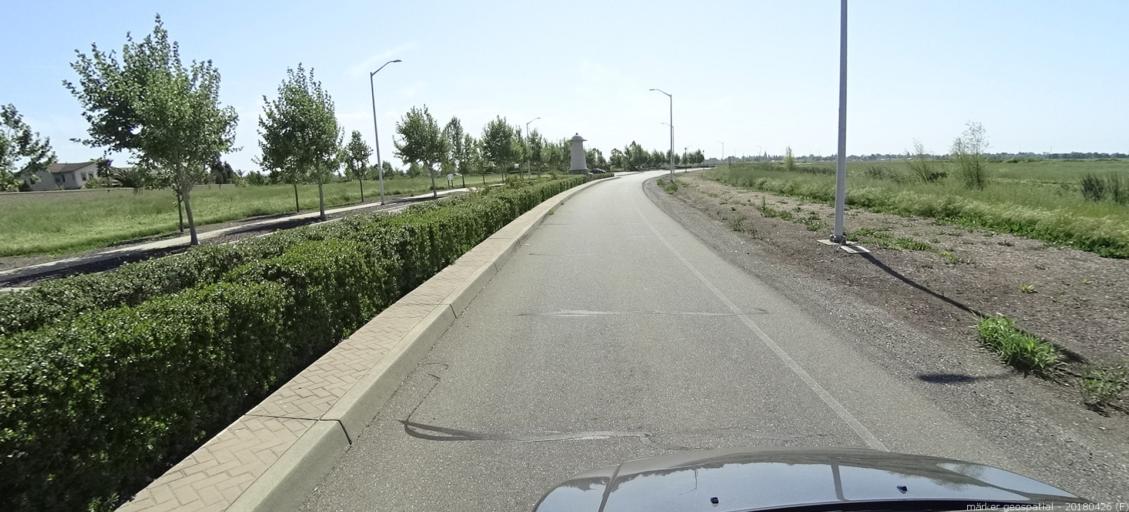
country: US
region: California
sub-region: Yolo County
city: West Sacramento
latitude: 38.5234
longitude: -121.5729
